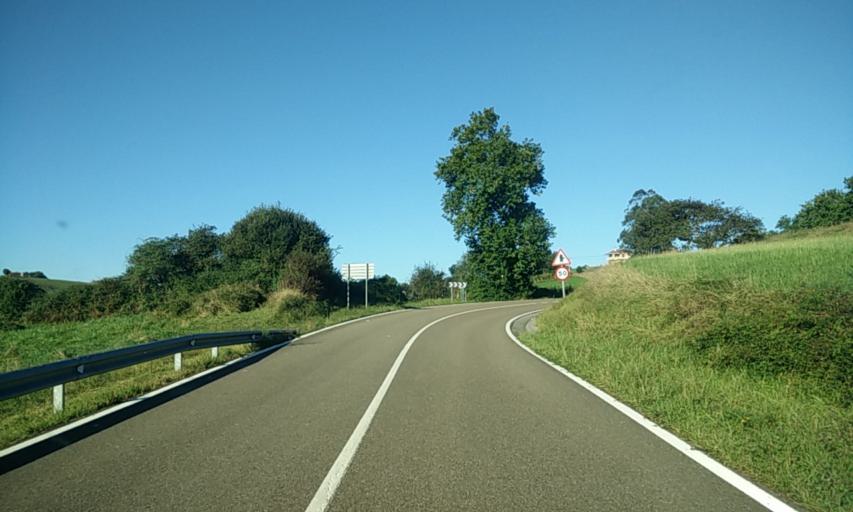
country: ES
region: Cantabria
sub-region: Provincia de Cantabria
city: San Vicente de la Barquera
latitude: 43.3818
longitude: -4.3515
